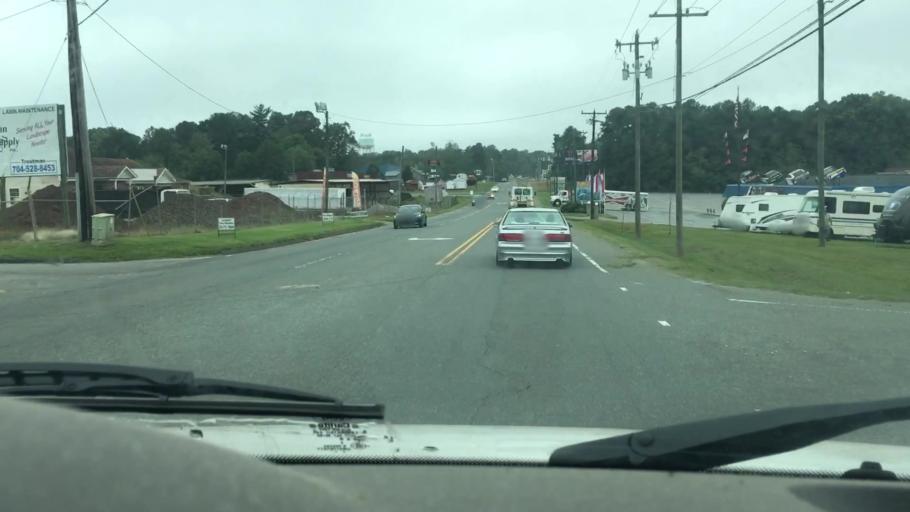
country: US
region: North Carolina
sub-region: Catawba County
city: Lake Norman of Catawba
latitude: 35.6040
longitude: -80.9089
